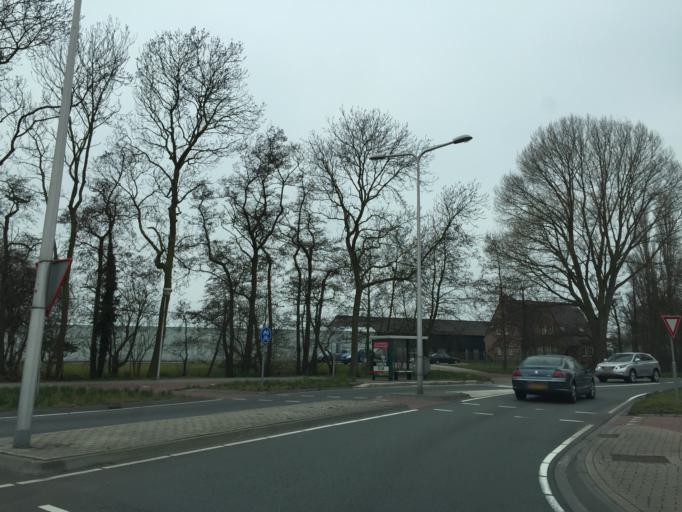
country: NL
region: South Holland
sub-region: Gemeente Westland
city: Naaldwijk
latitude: 51.9833
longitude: 4.2061
